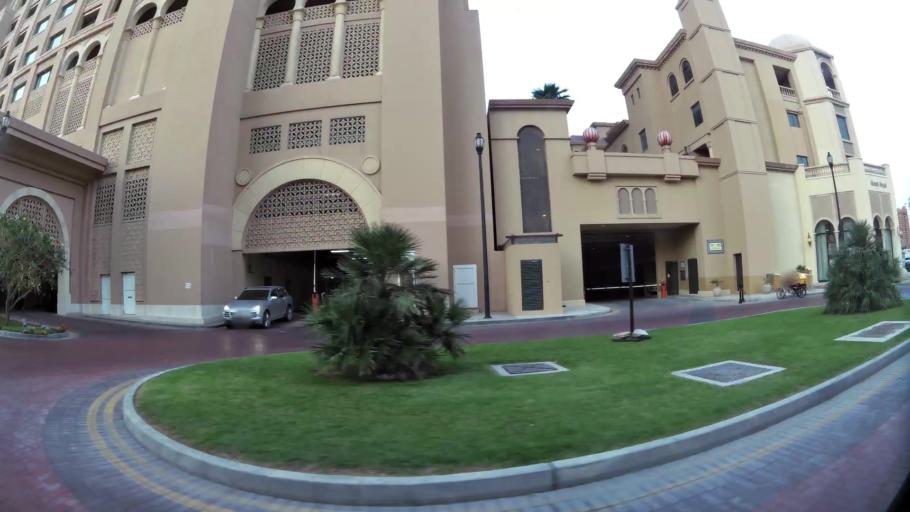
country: QA
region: Baladiyat ad Dawhah
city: Doha
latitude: 25.3719
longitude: 51.5401
